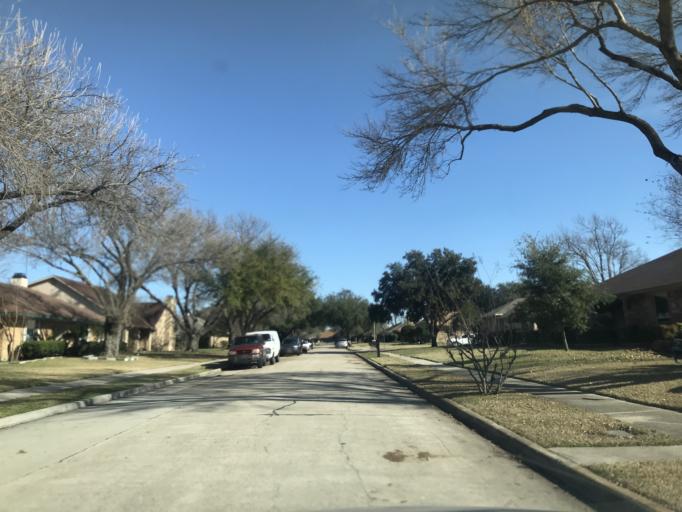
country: US
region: Texas
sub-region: Dallas County
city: Carrollton
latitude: 32.9874
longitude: -96.8727
